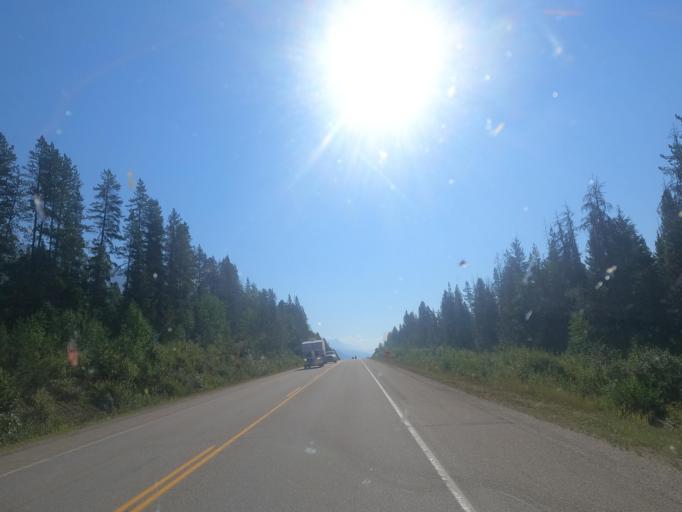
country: CA
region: Alberta
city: Jasper Park Lodge
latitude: 52.9770
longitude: -118.9664
